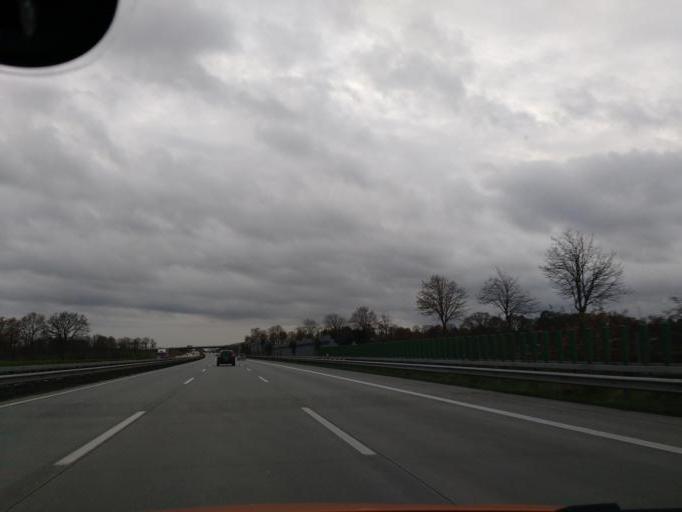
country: DE
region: Lower Saxony
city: Gyhum
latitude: 53.2209
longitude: 9.3226
